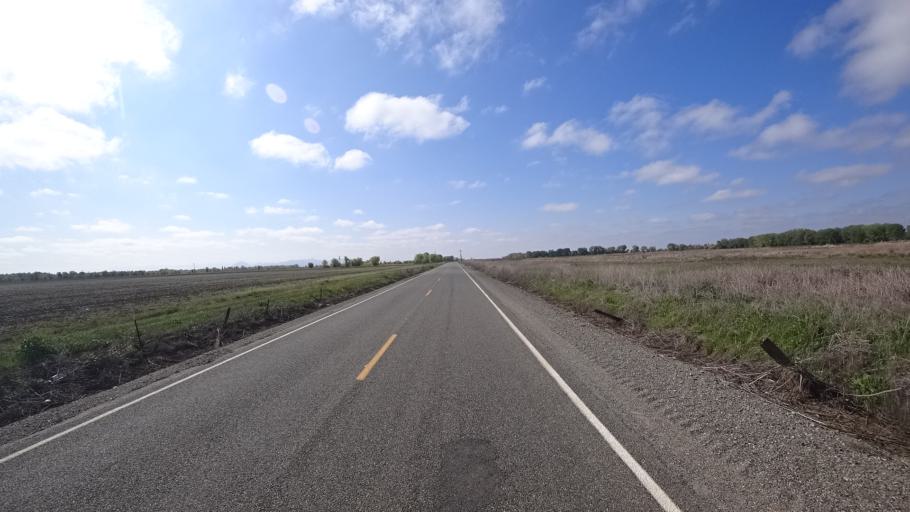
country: US
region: California
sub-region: Colusa County
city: Colusa
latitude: 39.4084
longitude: -121.9293
